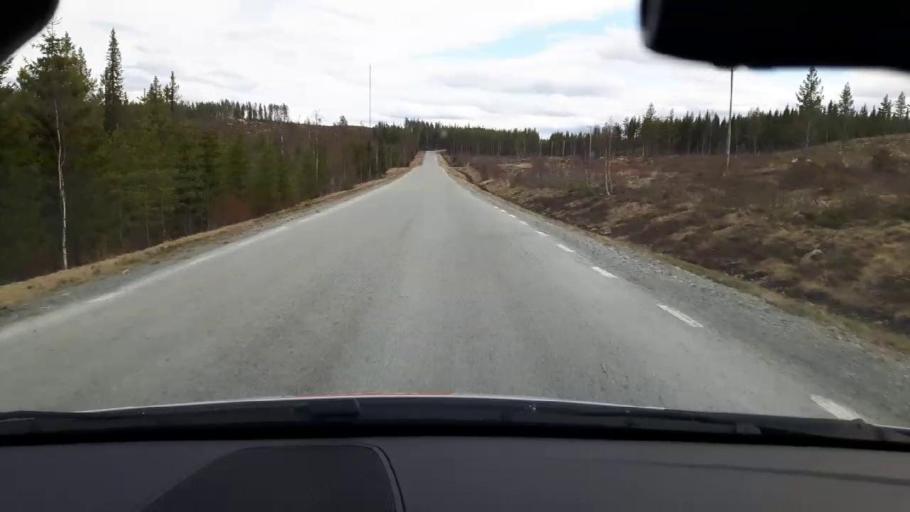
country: SE
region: Jaemtland
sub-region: Bergs Kommun
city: Hoverberg
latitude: 62.7089
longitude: 14.6129
